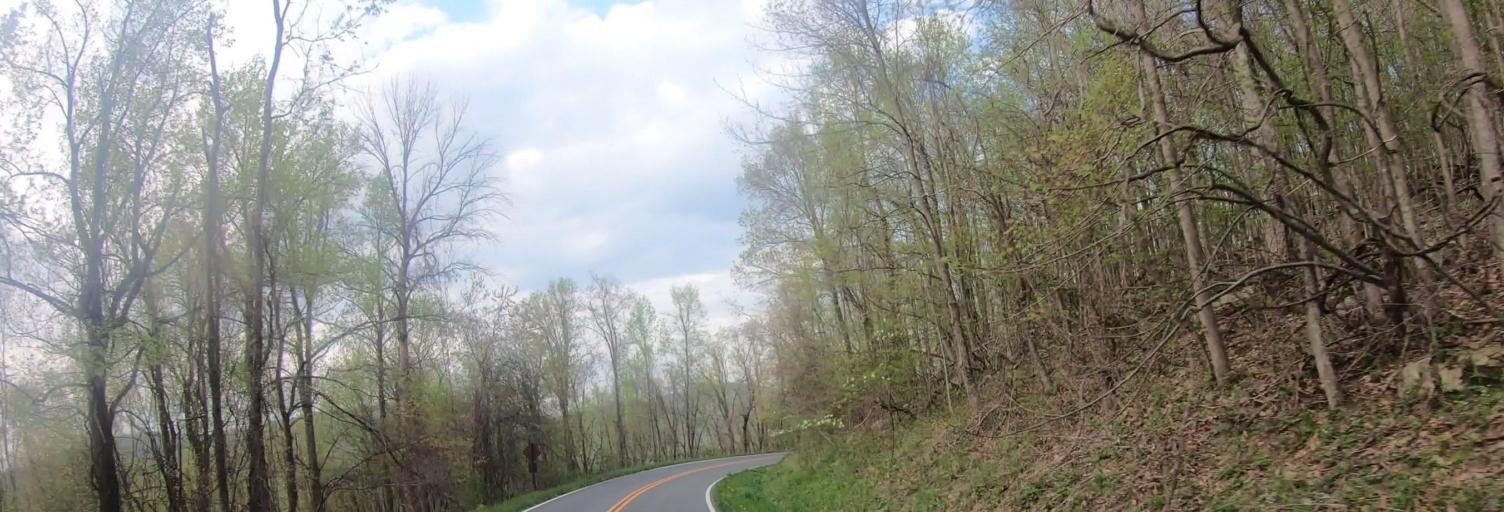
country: US
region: Virginia
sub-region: Augusta County
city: Dooms
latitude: 38.0834
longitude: -78.7939
